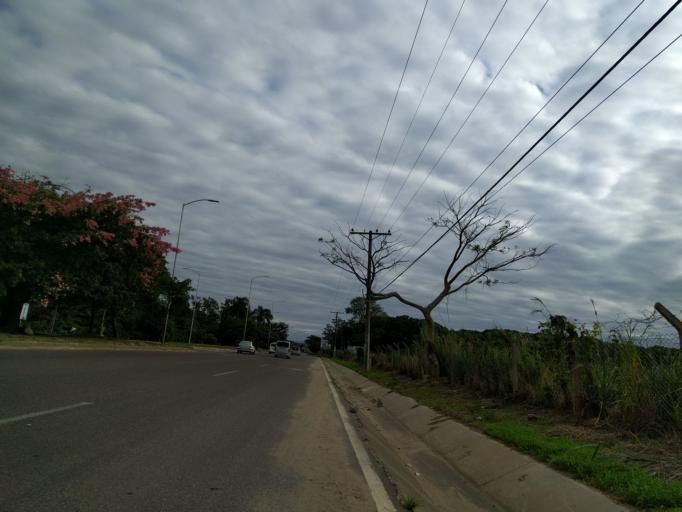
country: BO
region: Santa Cruz
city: Santa Cruz de la Sierra
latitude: -17.8663
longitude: -63.2700
